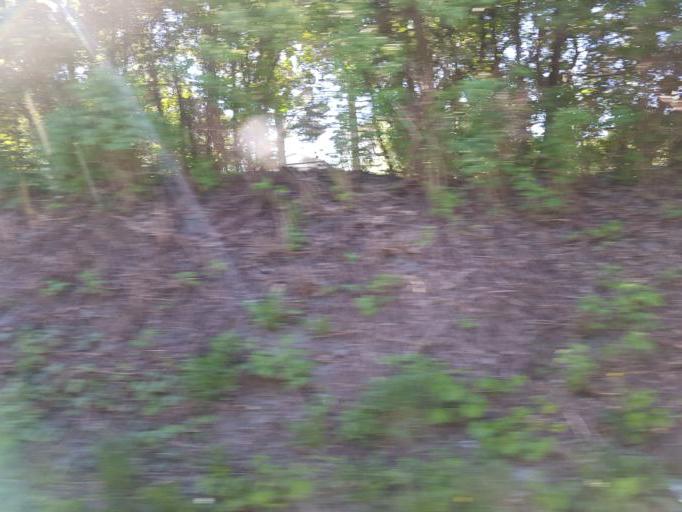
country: NO
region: Sor-Trondelag
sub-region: Trondheim
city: Trondheim
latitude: 63.4275
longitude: 10.5001
